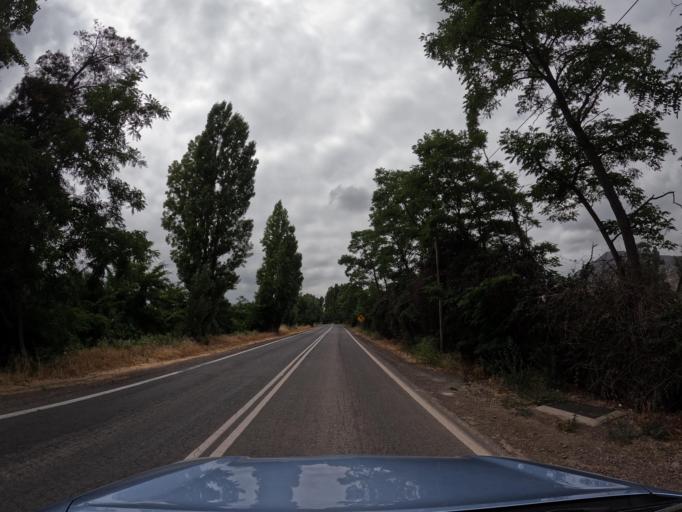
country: CL
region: Maule
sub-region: Provincia de Curico
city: Teno
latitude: -34.7512
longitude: -71.2256
